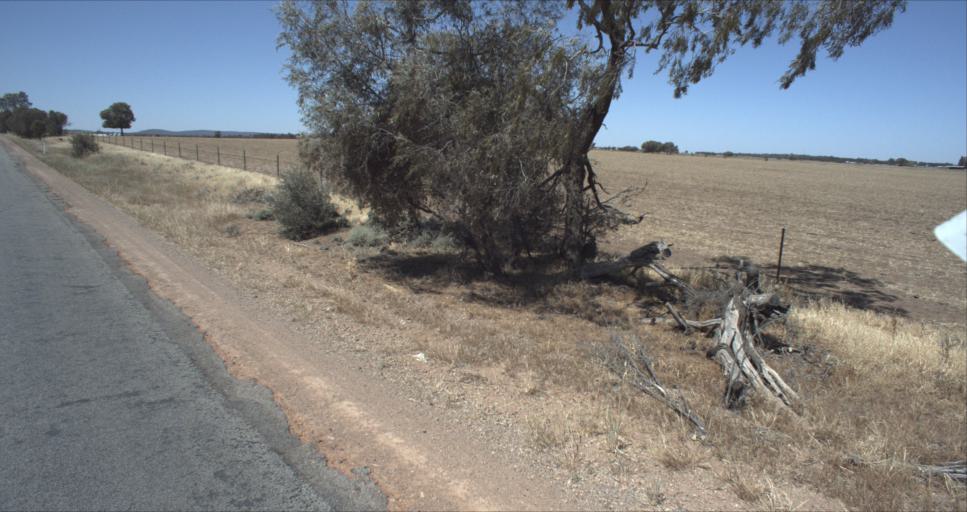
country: AU
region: New South Wales
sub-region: Leeton
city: Leeton
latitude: -34.5417
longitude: 146.4353
